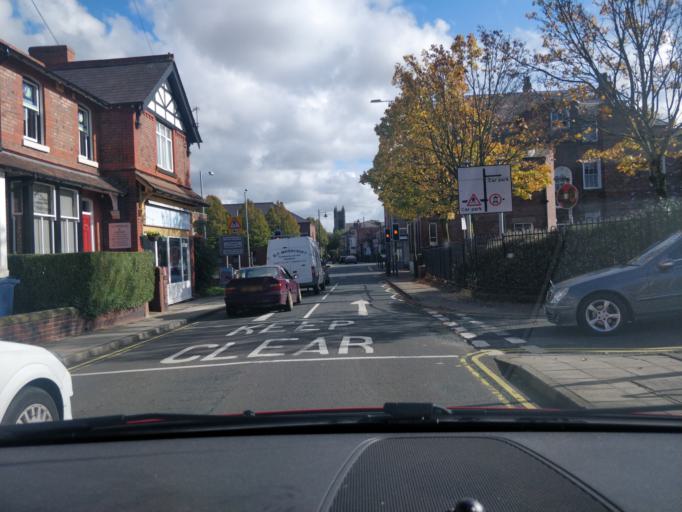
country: GB
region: England
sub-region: Lancashire
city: Ormskirk
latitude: 53.5690
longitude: -2.8857
